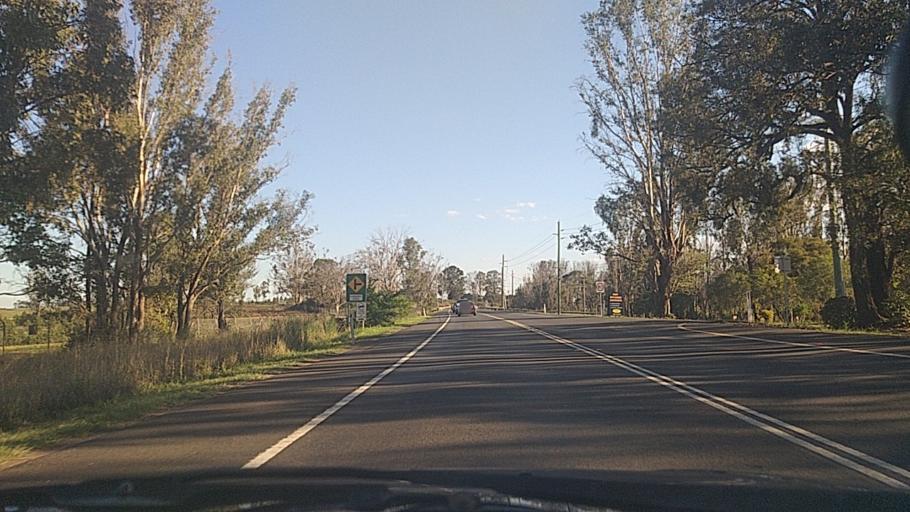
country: AU
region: New South Wales
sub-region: Penrith Municipality
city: Mulgoa
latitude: -33.8283
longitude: 150.6832
